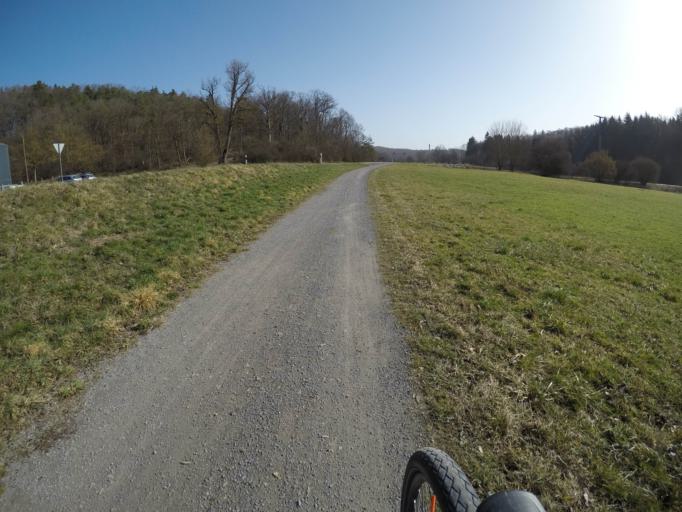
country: DE
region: Baden-Wuerttemberg
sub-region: Regierungsbezirk Stuttgart
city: Schonaich
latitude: 48.6518
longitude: 9.0874
